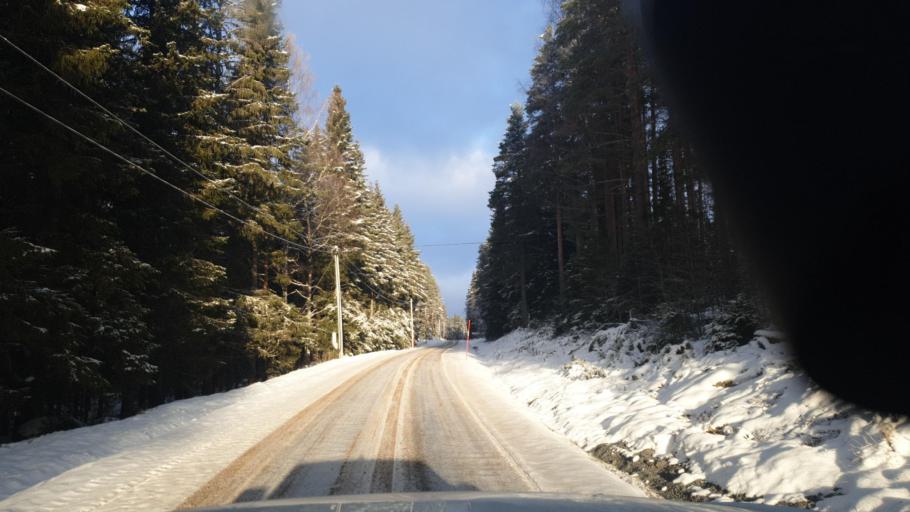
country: SE
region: Vaermland
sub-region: Eda Kommun
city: Charlottenberg
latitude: 60.1488
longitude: 12.5953
